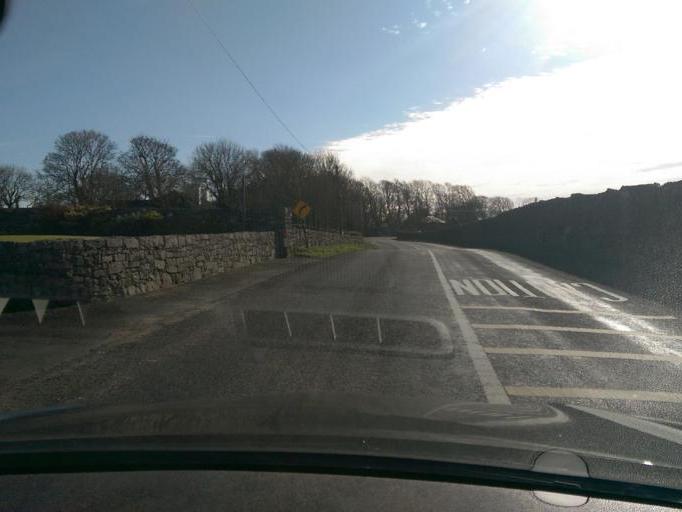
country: IE
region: Connaught
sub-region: County Galway
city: Oranmore
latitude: 53.2533
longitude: -8.9380
